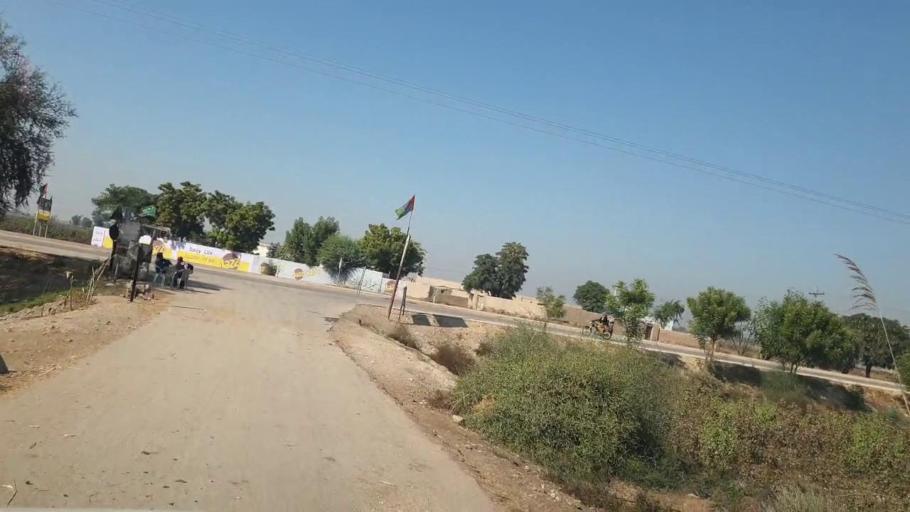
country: PK
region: Sindh
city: Bhan
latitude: 26.6106
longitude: 67.7329
